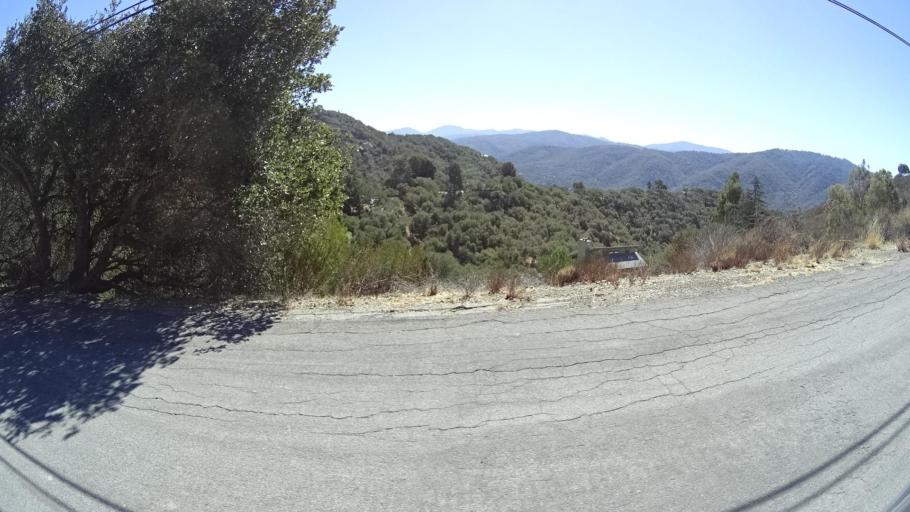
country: US
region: California
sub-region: Monterey County
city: Carmel Valley Village
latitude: 36.4951
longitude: -121.7317
